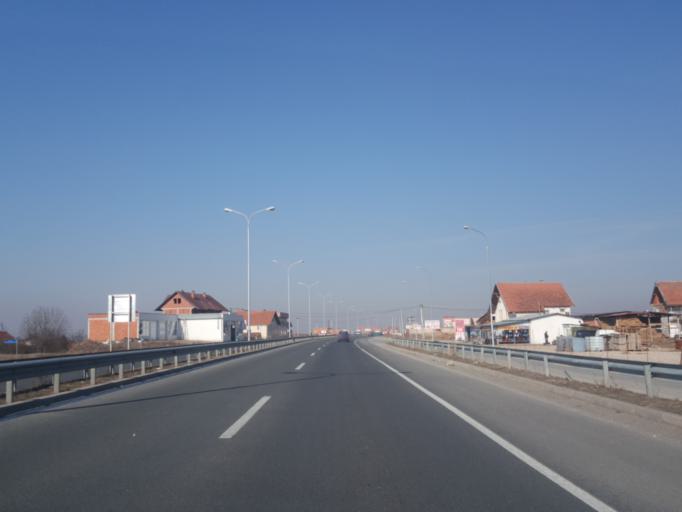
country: XK
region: Pristina
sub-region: Komuna e Obiliqit
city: Obiliq
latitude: 42.7403
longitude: 21.0526
